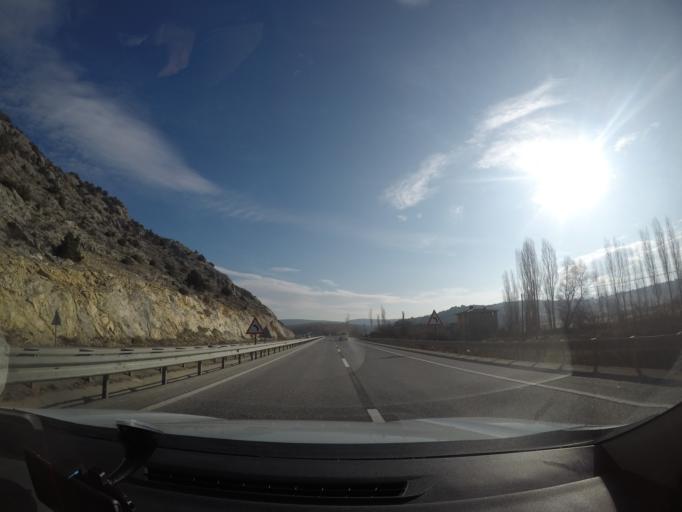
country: TR
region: Bilecik
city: Bozuyuk
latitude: 39.8939
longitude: 29.9734
